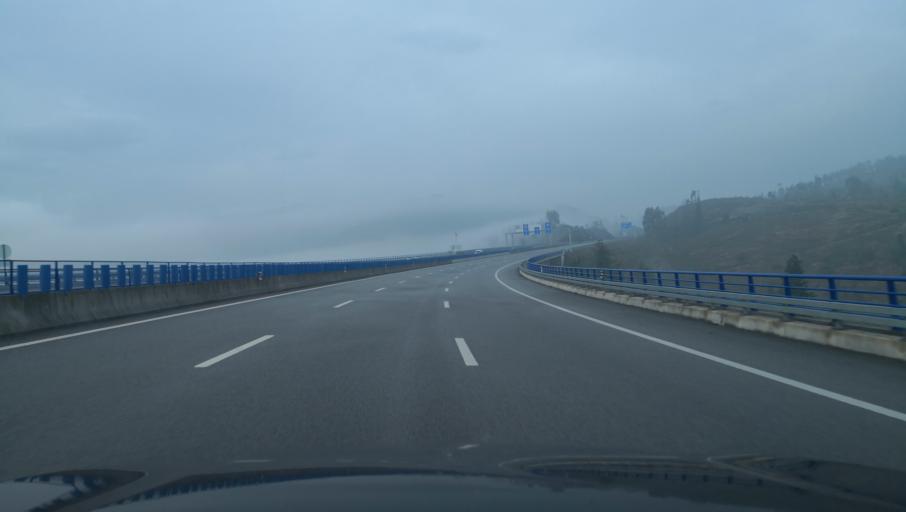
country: PT
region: Porto
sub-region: Paredes
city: Recarei
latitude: 41.1355
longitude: -8.4258
